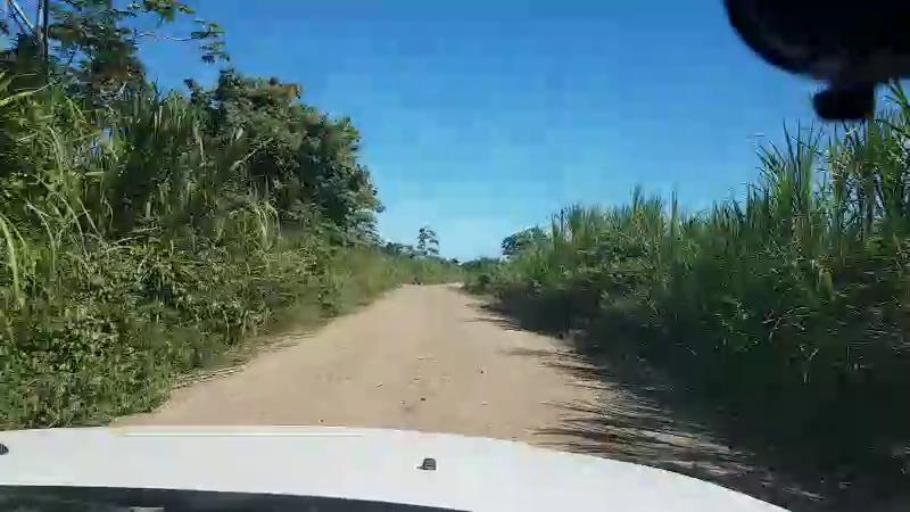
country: BZ
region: Stann Creek
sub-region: Dangriga
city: Dangriga
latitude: 17.1582
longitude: -88.3326
